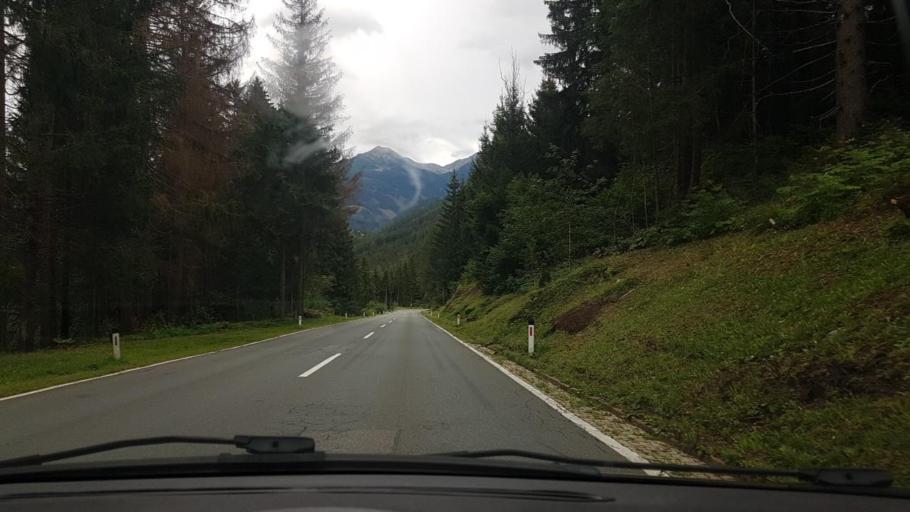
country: AT
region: Carinthia
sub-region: Politischer Bezirk Spittal an der Drau
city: Winklern
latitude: 46.8641
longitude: 12.8717
